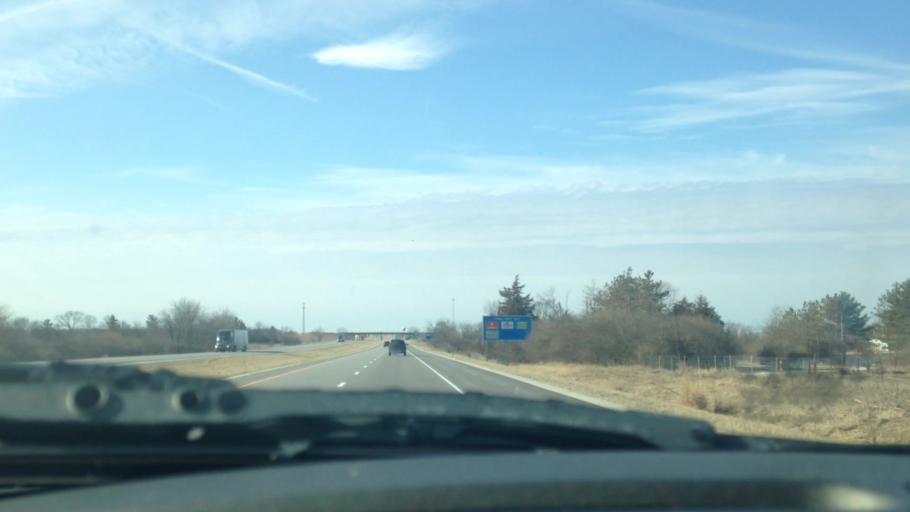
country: US
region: Illinois
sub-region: Ford County
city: Paxton
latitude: 40.4812
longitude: -88.1001
